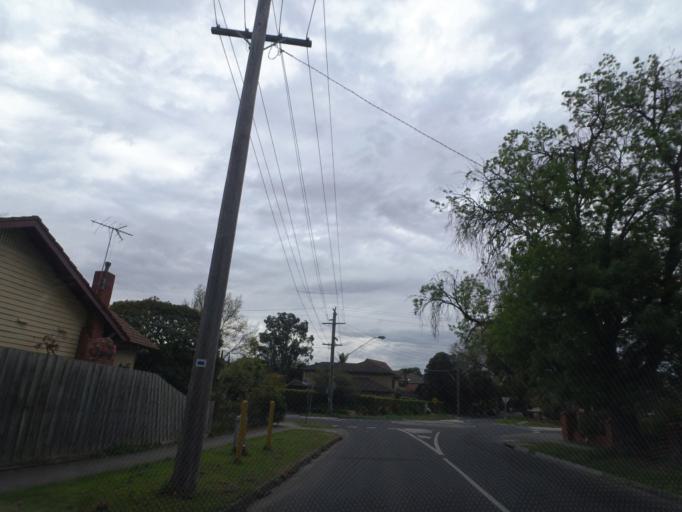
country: AU
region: Victoria
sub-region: Boroondara
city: Ashburton
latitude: -37.8665
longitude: 145.0675
